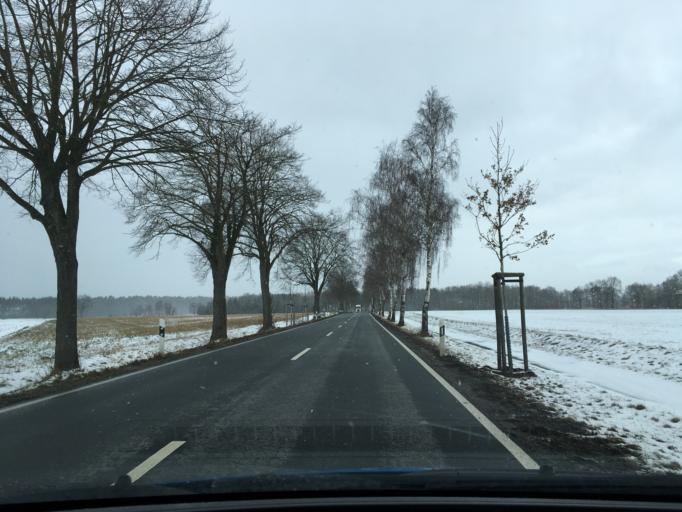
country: DE
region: Lower Saxony
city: Vierhofen
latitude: 53.2825
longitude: 10.2085
